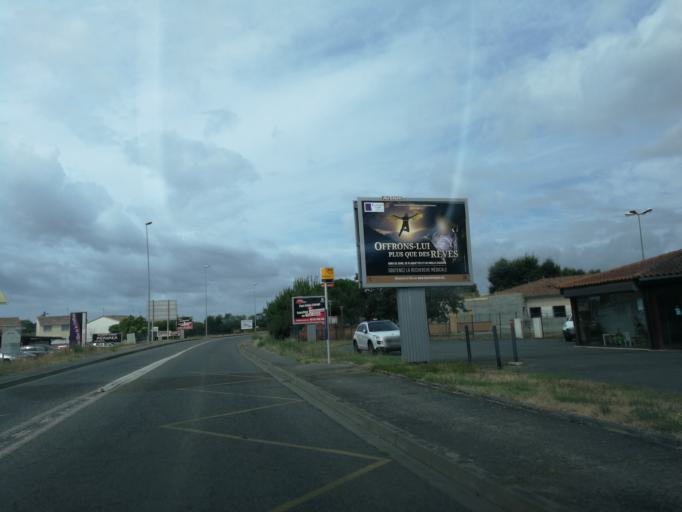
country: FR
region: Midi-Pyrenees
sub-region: Departement de la Haute-Garonne
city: Saint-Alban
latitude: 43.6877
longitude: 1.4160
